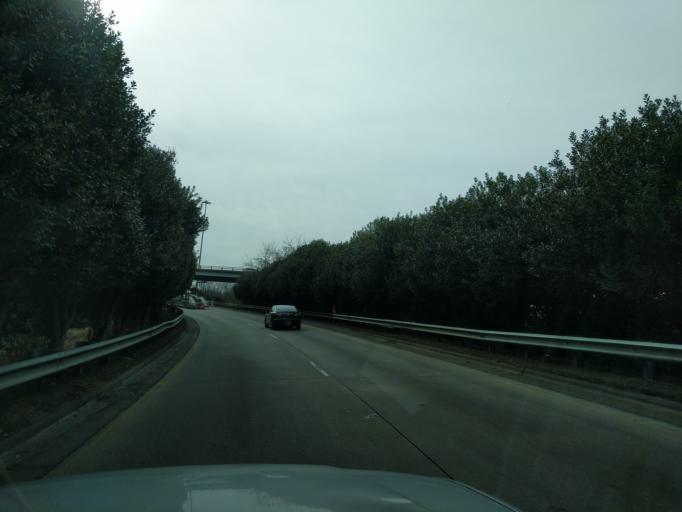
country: US
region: North Carolina
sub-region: Mecklenburg County
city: Charlotte
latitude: 35.2230
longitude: -80.8291
